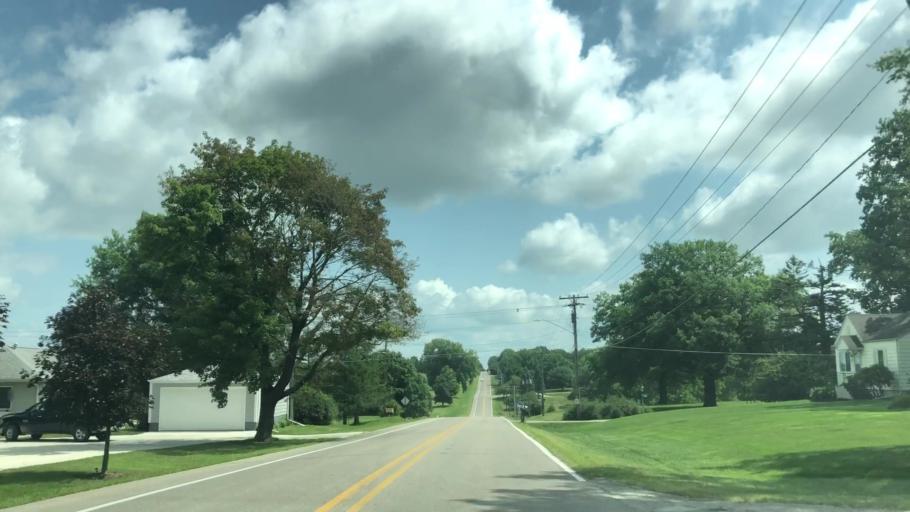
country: US
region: Iowa
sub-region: Marshall County
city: Marshalltown
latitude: 42.0286
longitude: -92.9324
